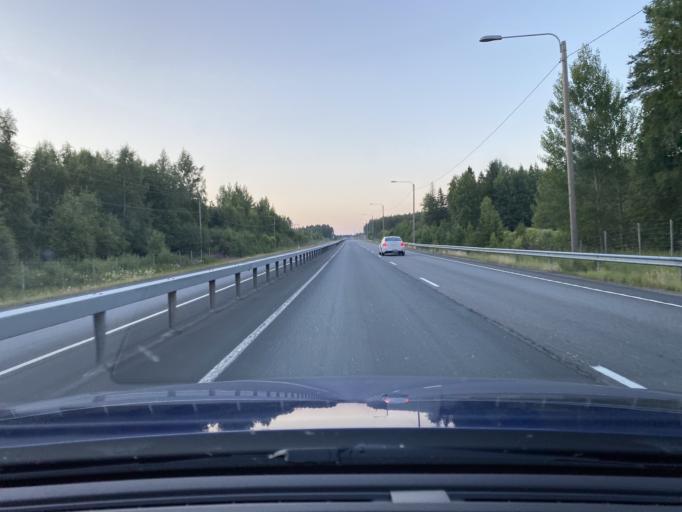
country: FI
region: Pirkanmaa
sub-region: Luoteis-Pirkanmaa
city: Parkano
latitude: 61.8833
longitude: 22.9727
